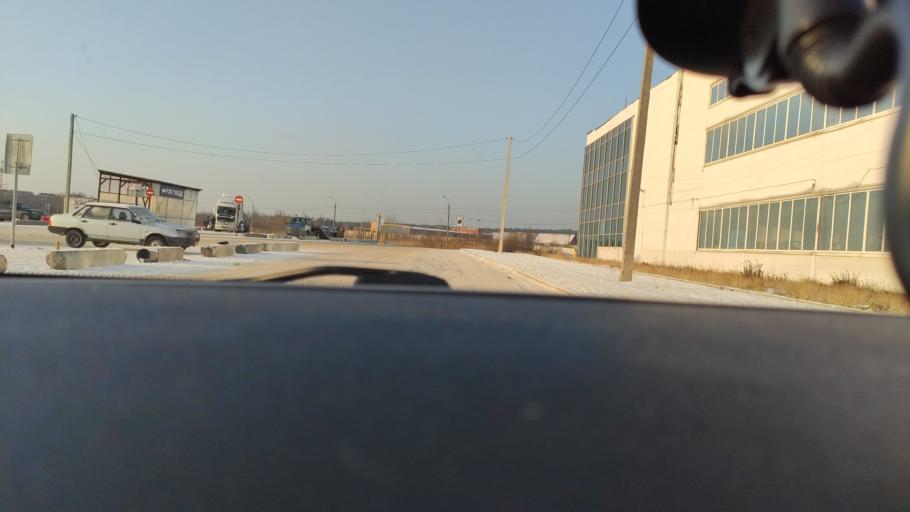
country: RU
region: Perm
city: Perm
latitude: 58.0345
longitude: 56.1968
